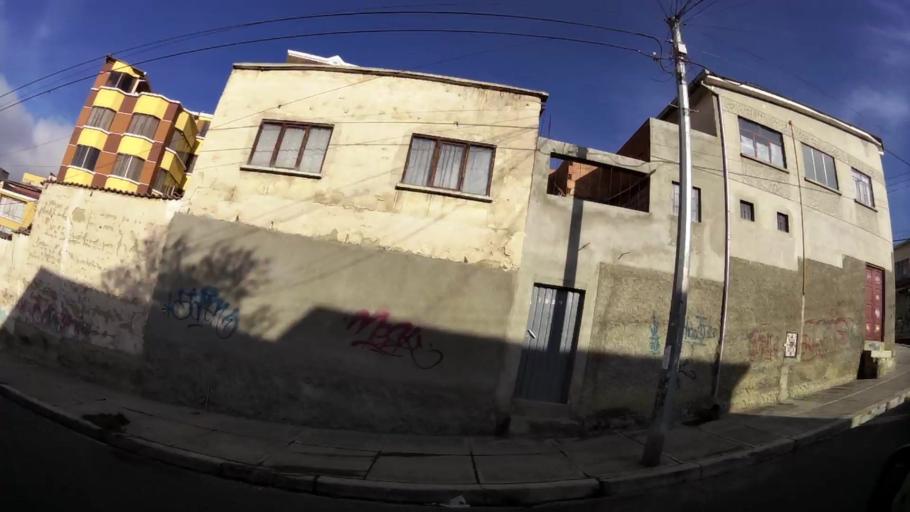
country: BO
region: La Paz
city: La Paz
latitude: -16.4894
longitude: -68.1242
